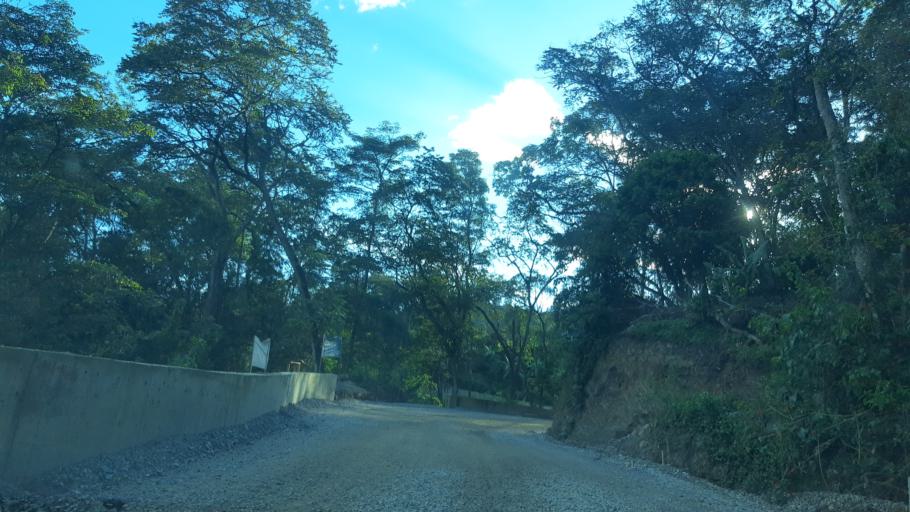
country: CO
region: Boyaca
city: Garagoa
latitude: 5.0867
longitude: -73.3849
